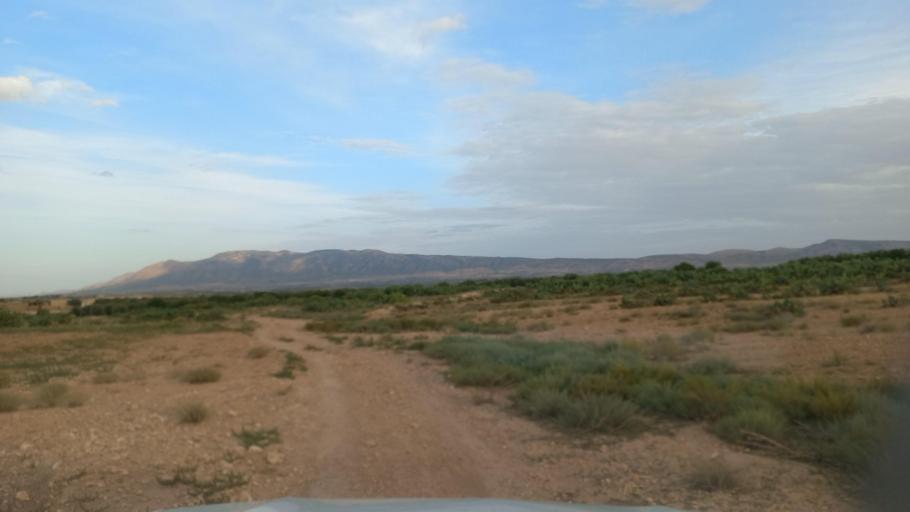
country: TN
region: Al Qasrayn
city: Sbiba
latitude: 35.4393
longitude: 9.0895
